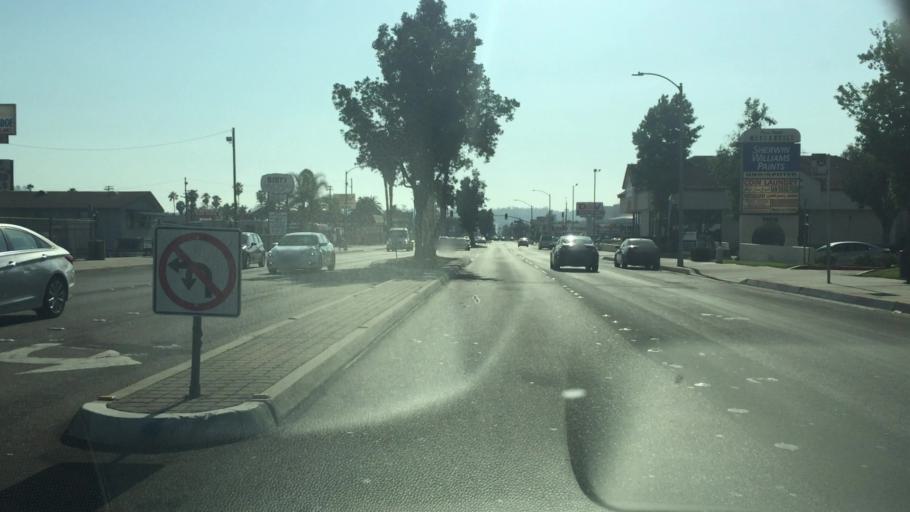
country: US
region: California
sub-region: San Diego County
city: Bostonia
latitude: 32.7950
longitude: -116.9424
